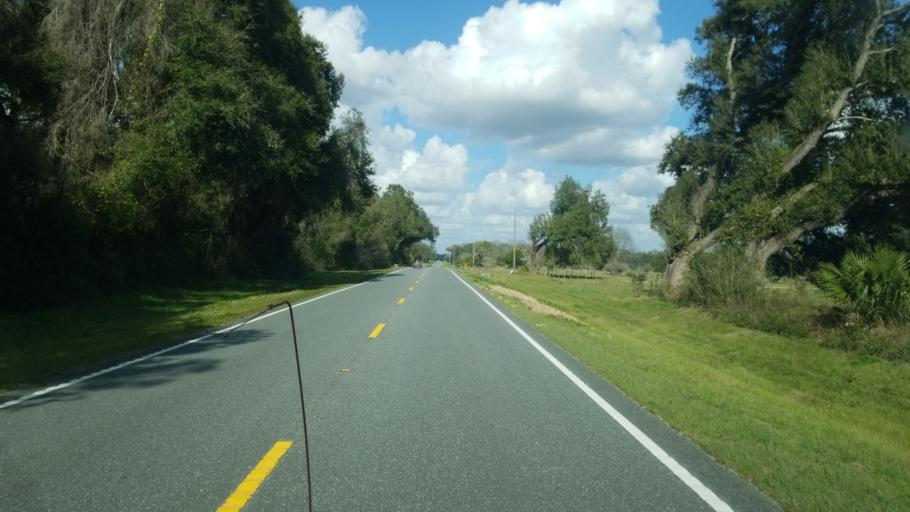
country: US
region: Florida
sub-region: Sumter County
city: Wildwood
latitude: 28.9111
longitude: -82.1200
